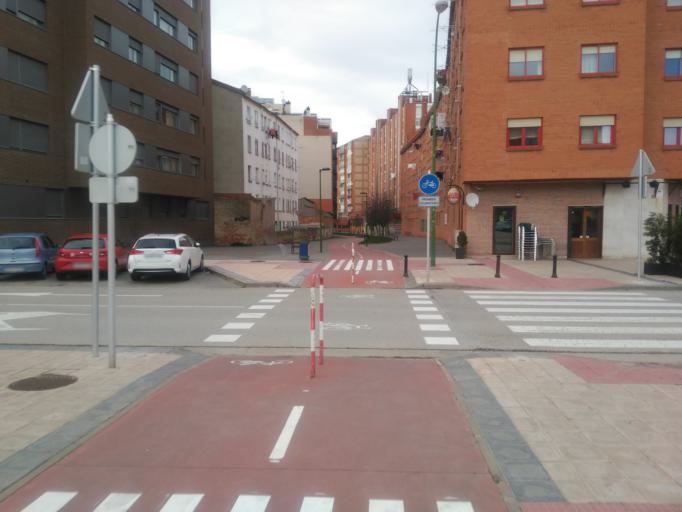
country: ES
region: Castille and Leon
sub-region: Provincia de Burgos
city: Burgos
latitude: 42.3305
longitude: -3.7010
